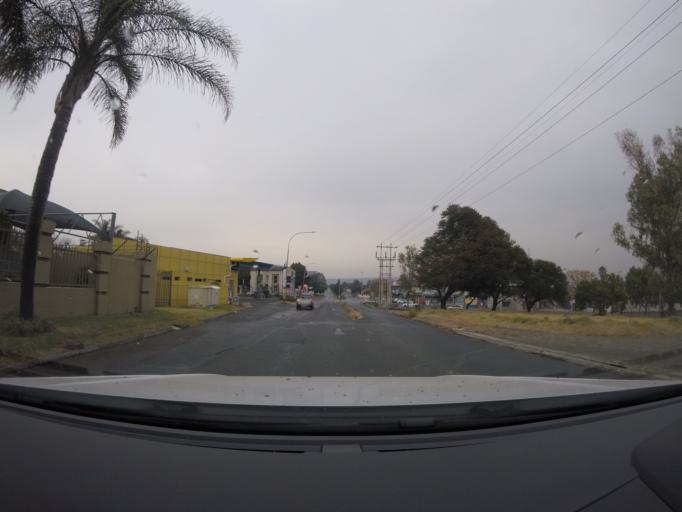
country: ZA
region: Gauteng
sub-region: City of Johannesburg Metropolitan Municipality
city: Modderfontein
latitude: -26.1493
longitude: 28.1505
